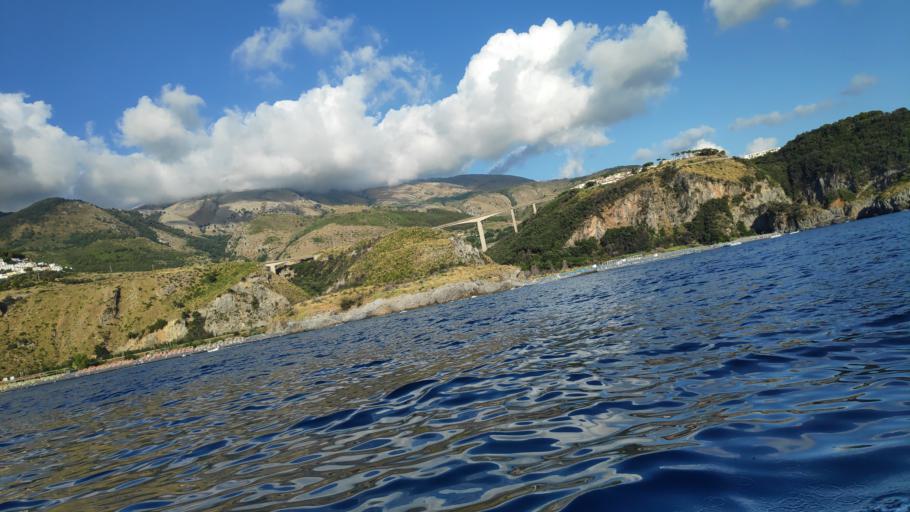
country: IT
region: Calabria
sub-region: Provincia di Cosenza
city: San Nicola Arcella
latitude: 39.8603
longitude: 15.7855
